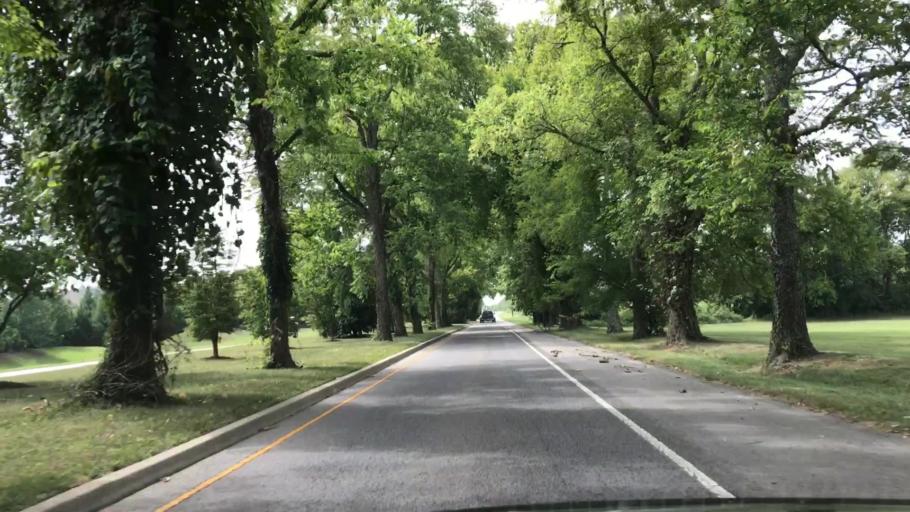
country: US
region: Tennessee
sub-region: Williamson County
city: Brentwood Estates
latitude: 35.9452
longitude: -86.7670
